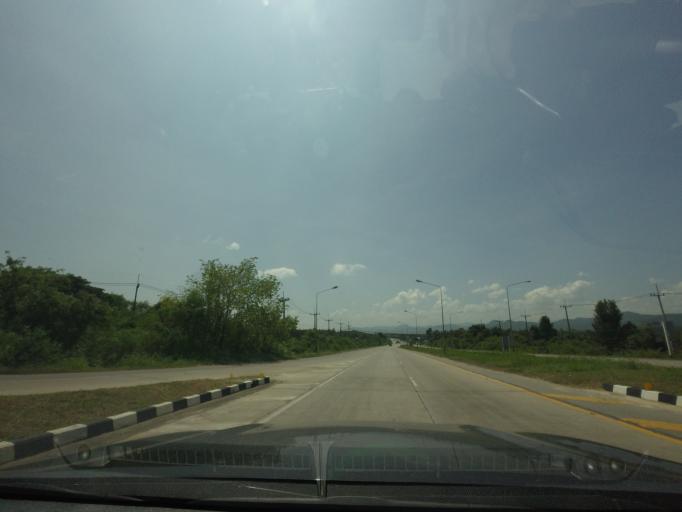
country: TH
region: Phetchabun
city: Lom Sak
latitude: 16.7647
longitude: 101.1853
